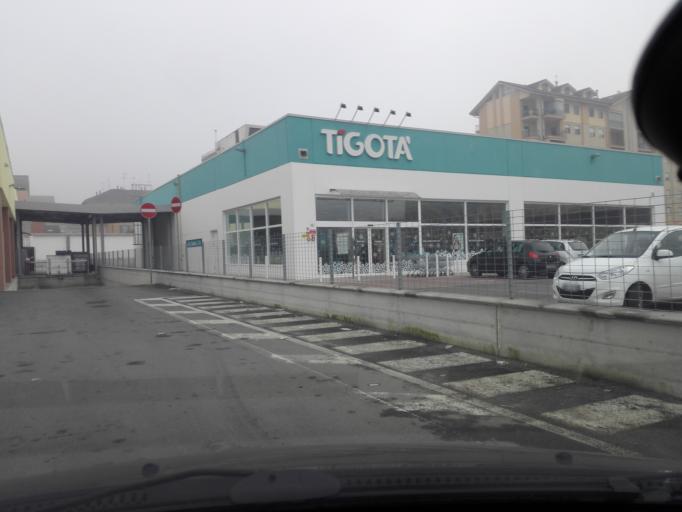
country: IT
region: Piedmont
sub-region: Provincia di Alessandria
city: Alessandria
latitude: 44.9004
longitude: 8.6087
